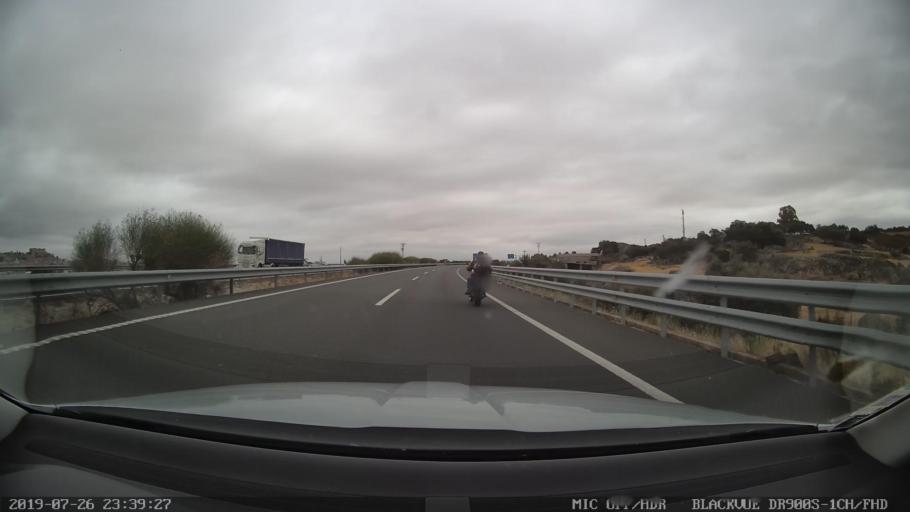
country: ES
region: Extremadura
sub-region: Provincia de Caceres
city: Trujillo
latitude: 39.4490
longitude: -5.8730
